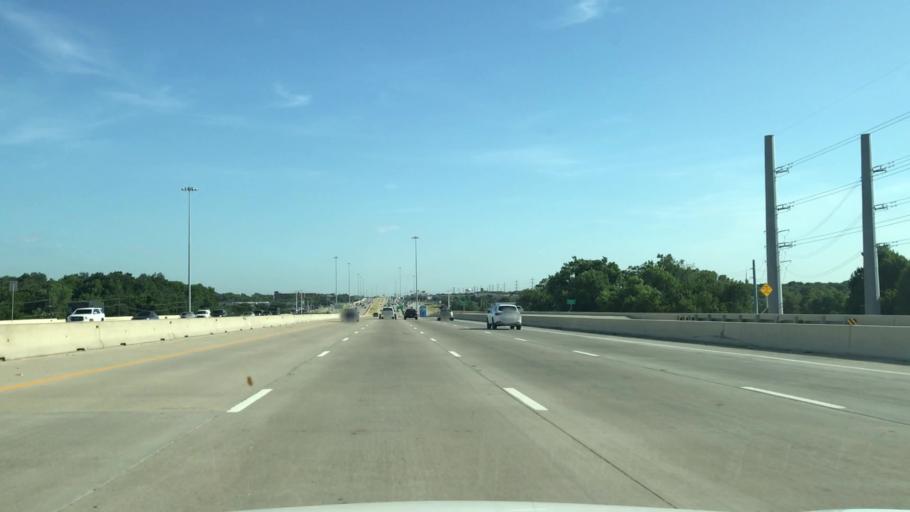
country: US
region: Texas
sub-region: Collin County
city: Fairview
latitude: 33.1833
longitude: -96.6396
